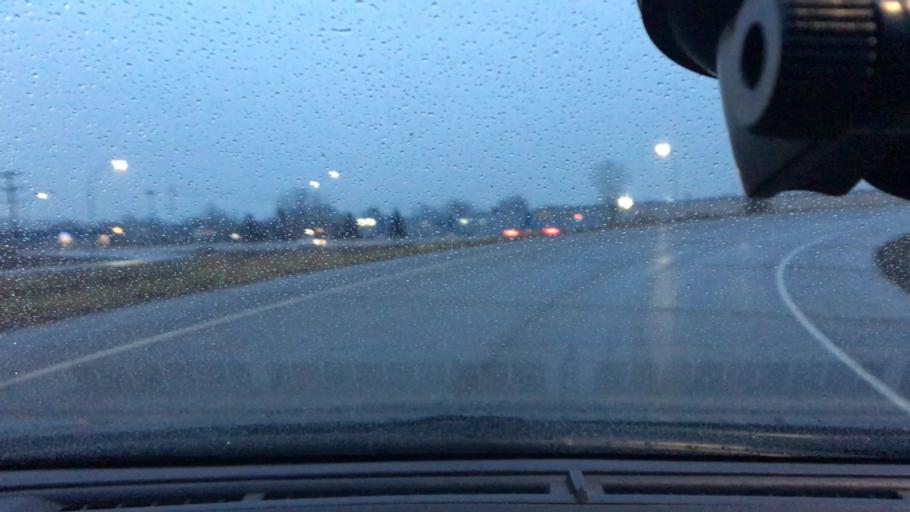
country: US
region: Minnesota
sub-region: Hennepin County
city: New Hope
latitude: 45.0588
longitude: -93.3994
